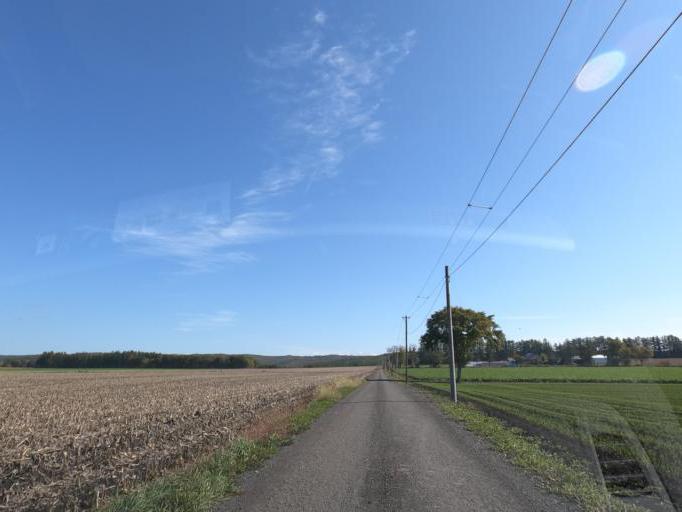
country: JP
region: Hokkaido
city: Otofuke
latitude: 43.0116
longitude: 143.2623
